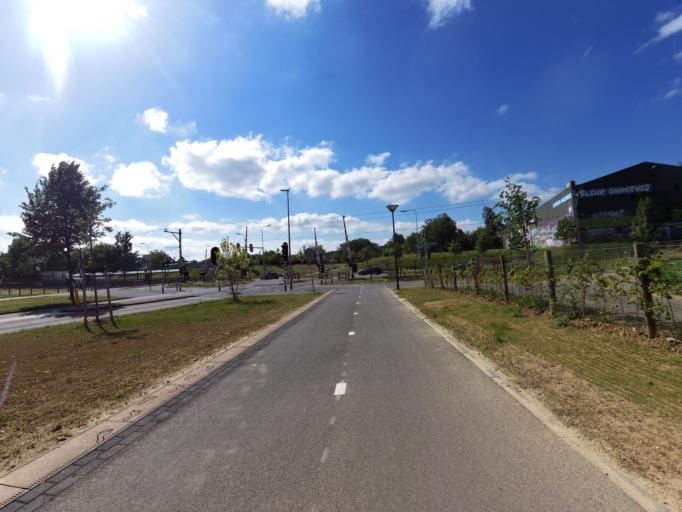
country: NL
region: Limburg
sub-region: Gemeente Heerlen
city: Heerlen
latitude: 50.8904
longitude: 5.9925
